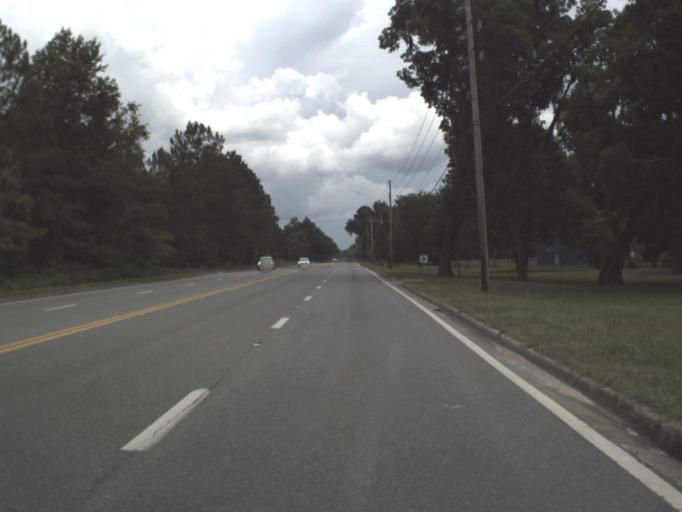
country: US
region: Florida
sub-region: Taylor County
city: Perry
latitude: 30.0955
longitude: -83.5459
